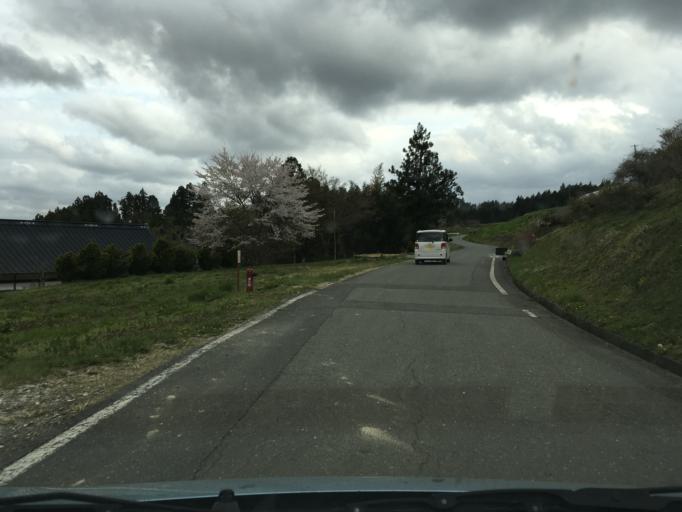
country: JP
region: Iwate
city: Ichinoseki
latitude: 38.9615
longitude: 141.2120
